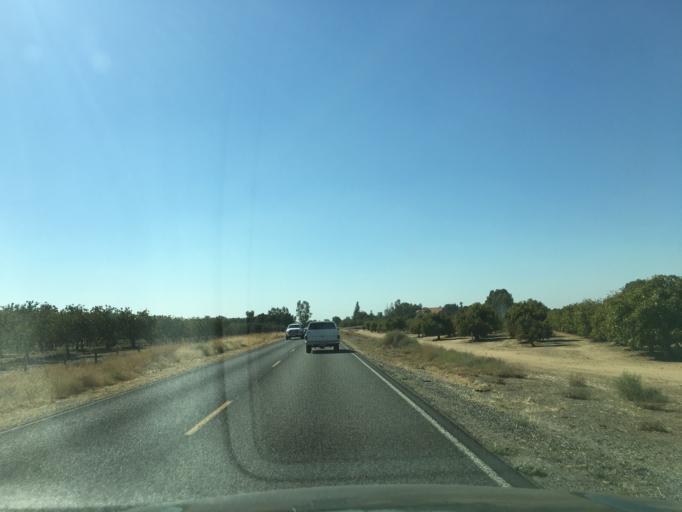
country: US
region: California
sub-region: Madera County
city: Parksdale
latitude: 37.0007
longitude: -119.9707
